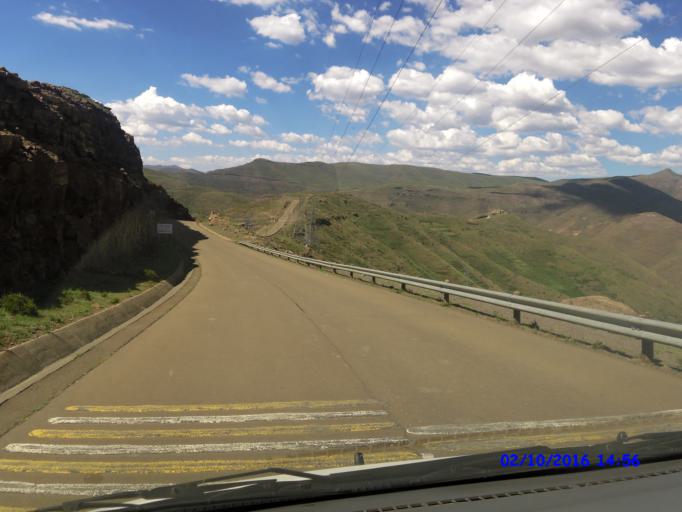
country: LS
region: Maseru
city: Nako
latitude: -29.4684
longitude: 28.0908
